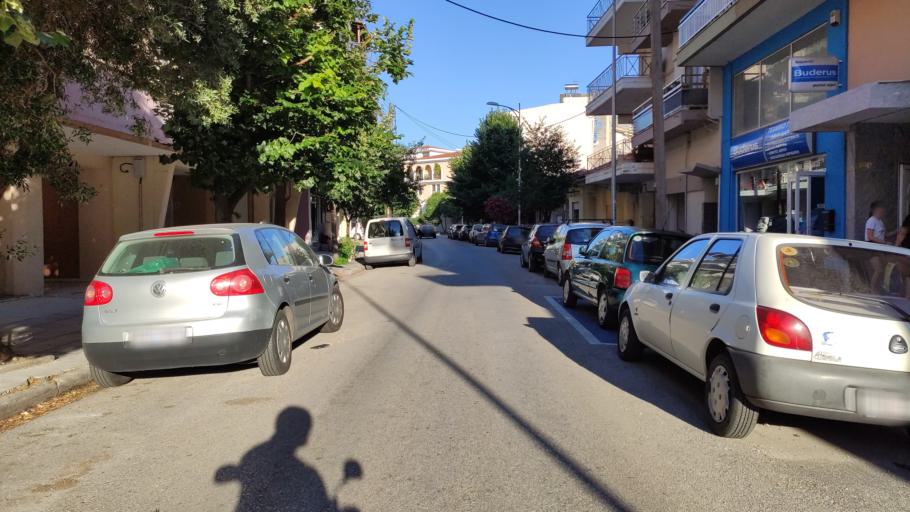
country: GR
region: East Macedonia and Thrace
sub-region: Nomos Rodopis
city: Komotini
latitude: 41.1179
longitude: 25.3949
